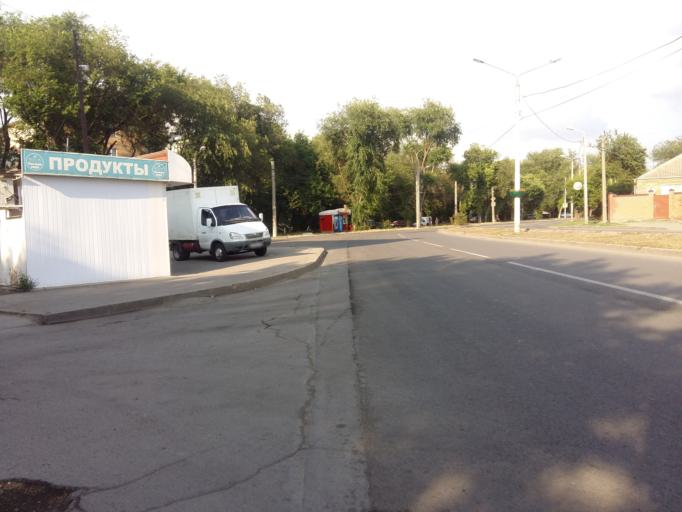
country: RU
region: Rostov
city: Imeni Chkalova
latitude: 47.2754
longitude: 39.7367
